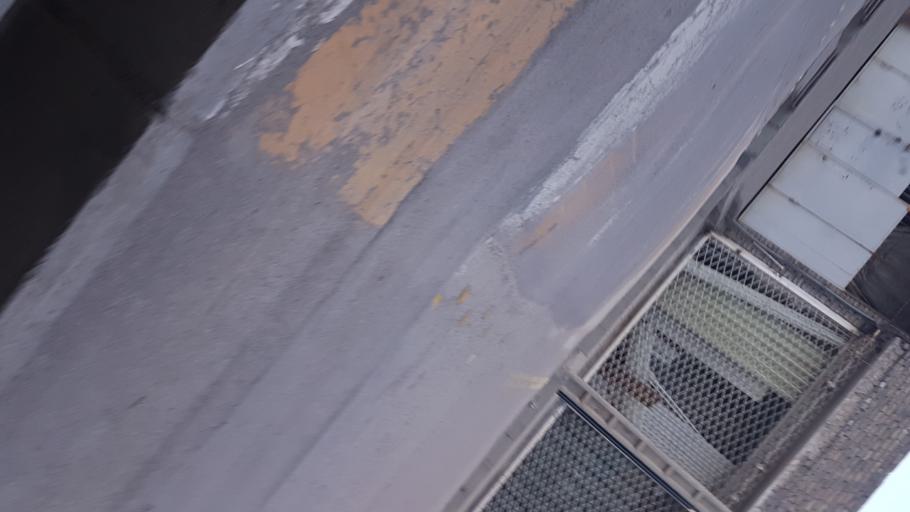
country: IR
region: Razavi Khorasan
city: Mashhad
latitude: 36.3512
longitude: 59.5786
